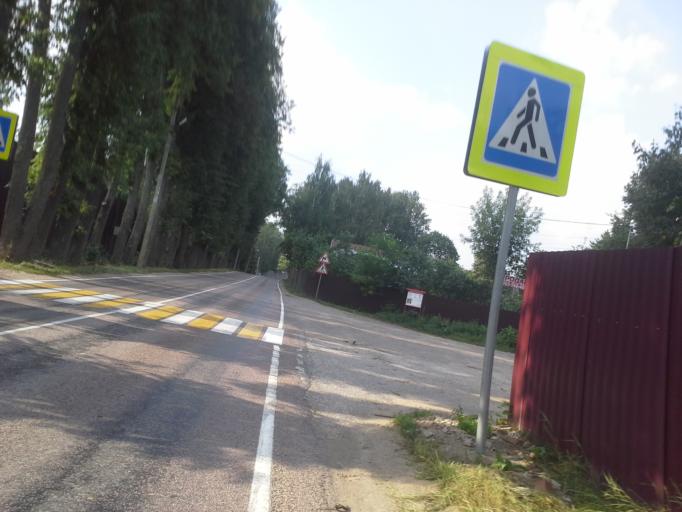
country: RU
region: Moskovskaya
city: Istra
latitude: 55.8922
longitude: 36.7953
